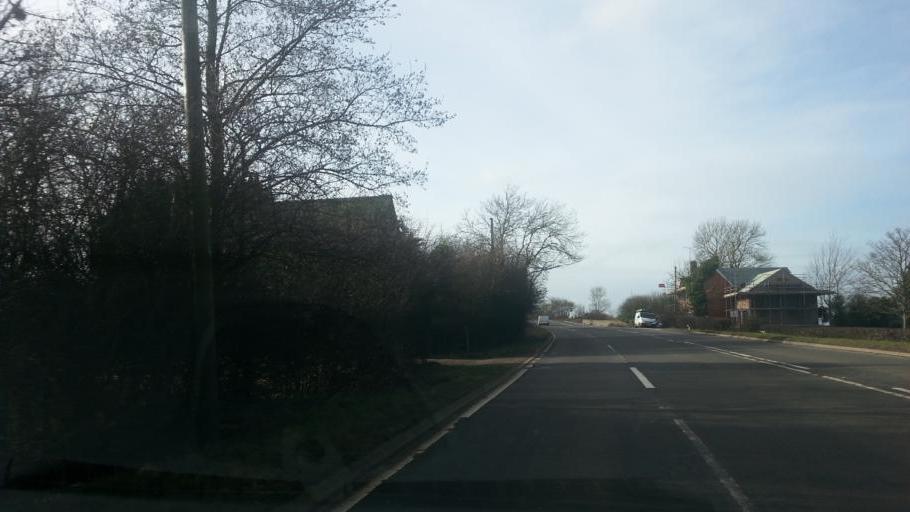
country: GB
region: England
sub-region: District of Rutland
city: Ridlington
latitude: 52.5945
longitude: -0.8292
